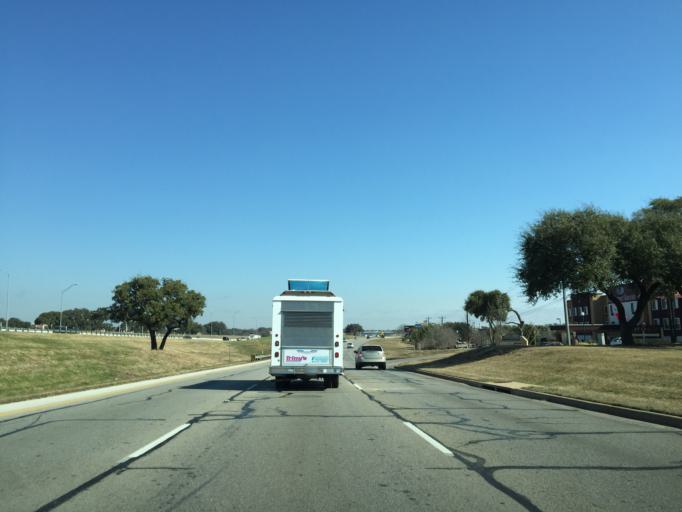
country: US
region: Texas
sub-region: Williamson County
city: Georgetown
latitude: 30.6411
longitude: -97.6874
